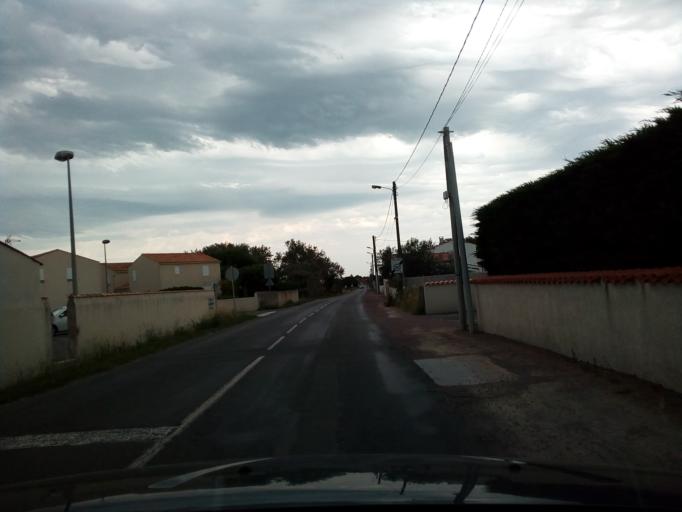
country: FR
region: Poitou-Charentes
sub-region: Departement de la Charente-Maritime
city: Dolus-d'Oleron
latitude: 45.9209
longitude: -1.3285
